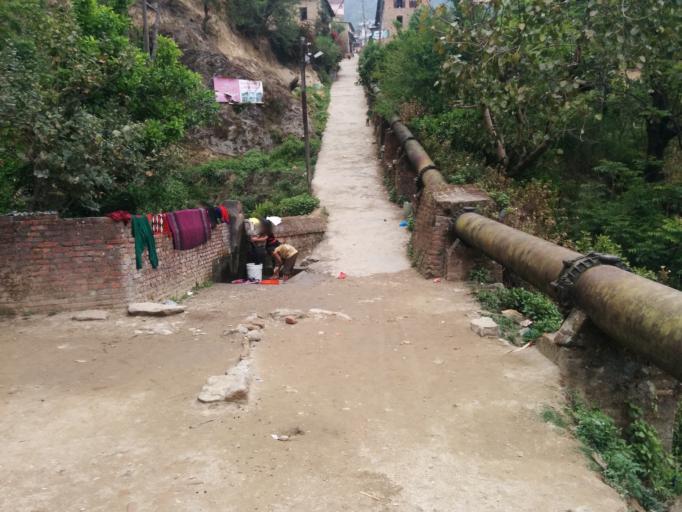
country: NP
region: Central Region
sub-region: Bagmati Zone
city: Bhaktapur
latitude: 27.7624
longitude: 85.4221
